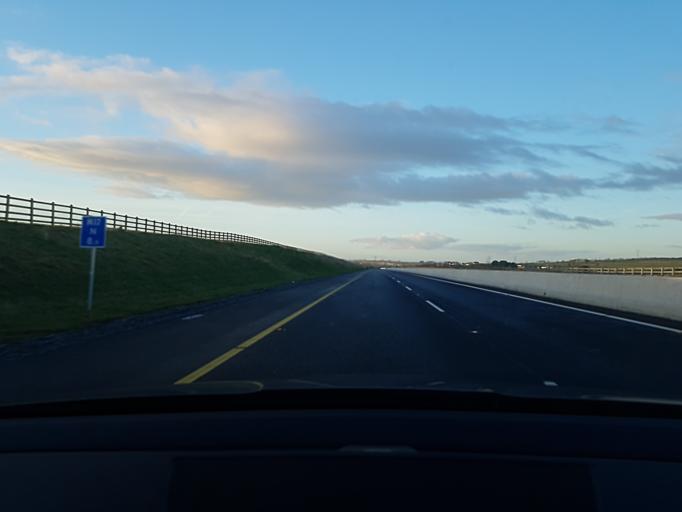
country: IE
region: Connaught
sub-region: County Galway
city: Athenry
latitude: 53.3702
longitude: -8.7906
